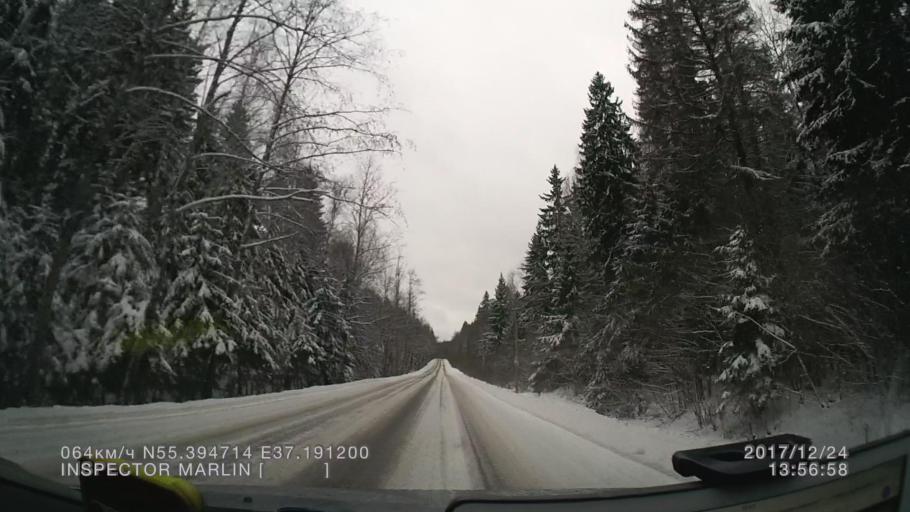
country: RU
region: Moskovskaya
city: Troitsk
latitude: 55.3946
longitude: 37.1910
